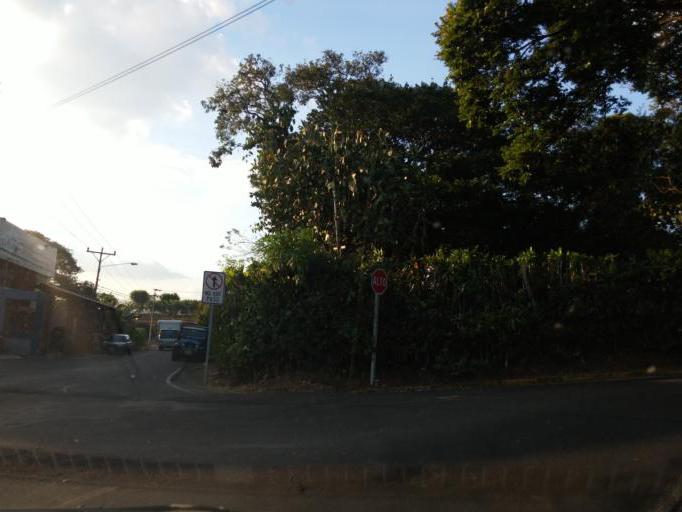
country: CR
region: Alajuela
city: Alajuela
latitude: 10.0139
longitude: -84.2248
